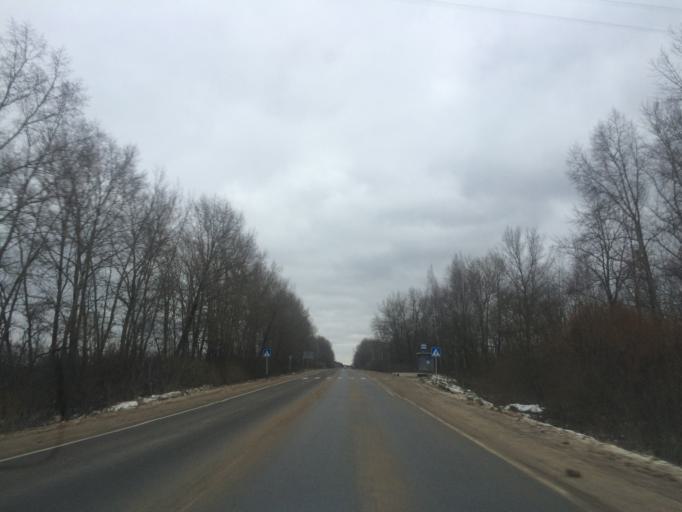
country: RU
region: Tula
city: Odoyev
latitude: 53.9894
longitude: 36.7182
